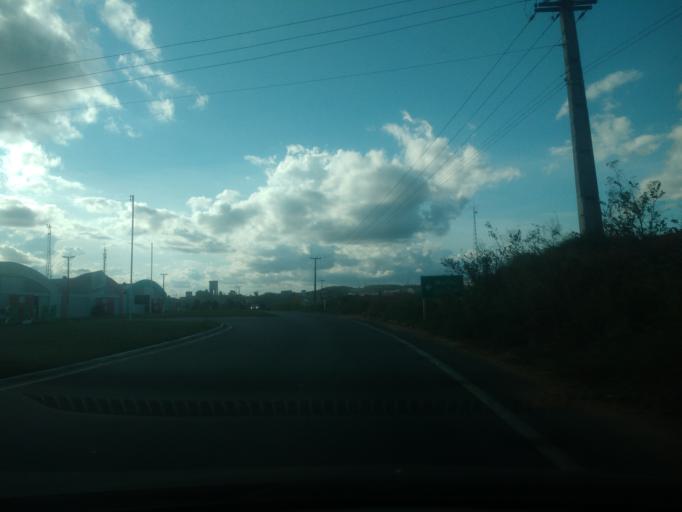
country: BR
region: Alagoas
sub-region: Murici
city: Murici
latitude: -9.3123
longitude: -35.9336
